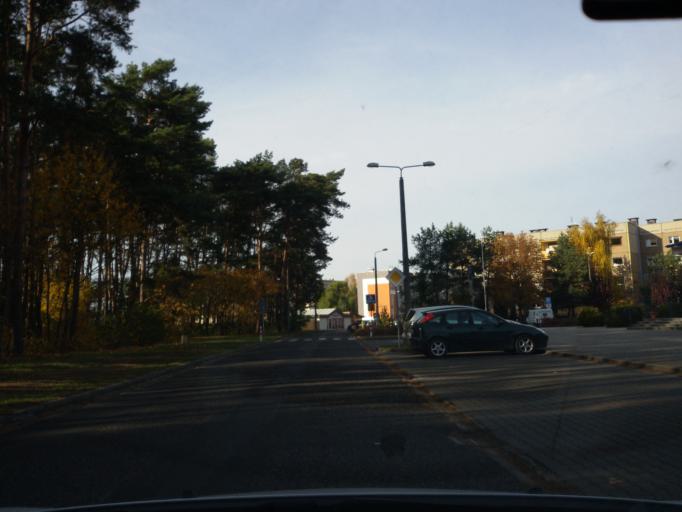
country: PL
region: Greater Poland Voivodeship
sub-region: Leszno
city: Leszno
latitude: 51.8321
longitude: 16.6021
